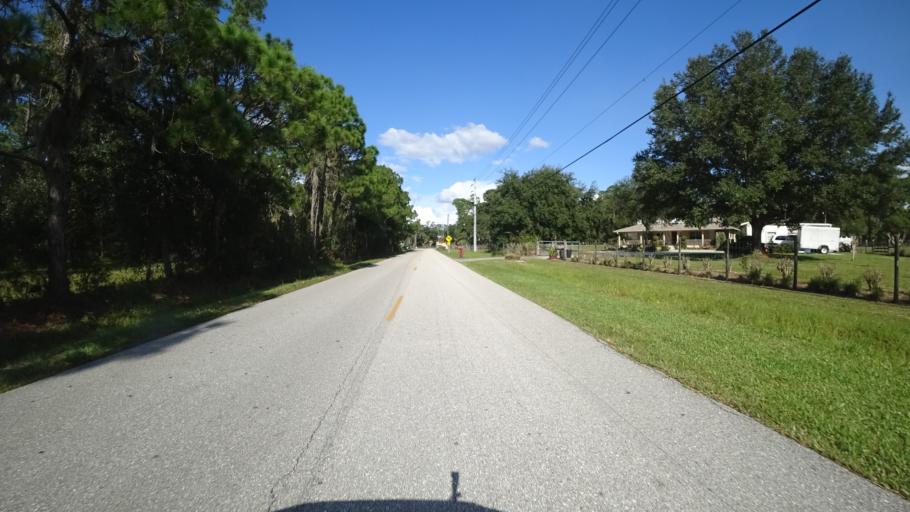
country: US
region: Florida
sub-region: Manatee County
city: Samoset
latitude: 27.4628
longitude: -82.4751
